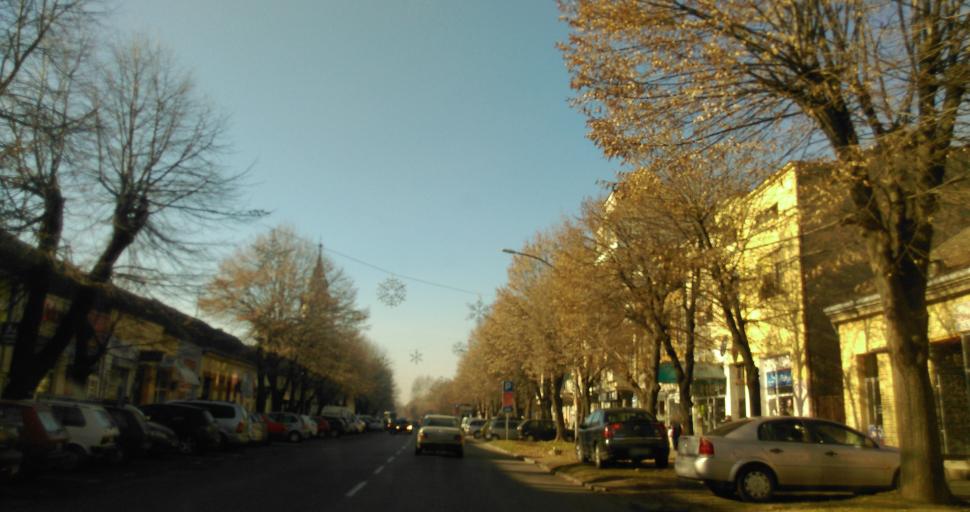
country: RS
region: Autonomna Pokrajina Vojvodina
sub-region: Sremski Okrug
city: Ruma
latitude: 45.0078
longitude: 19.8265
